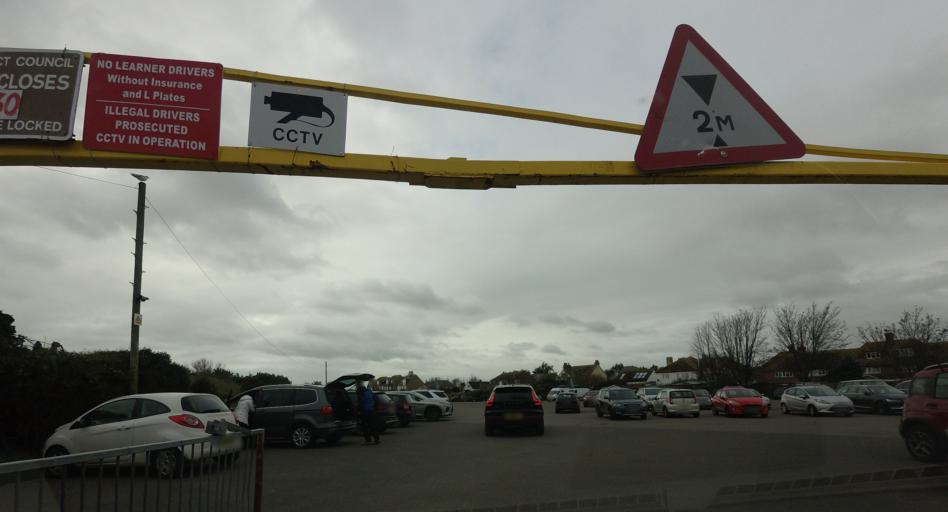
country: GB
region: England
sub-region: East Sussex
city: Rye
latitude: 50.9370
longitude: 0.7627
